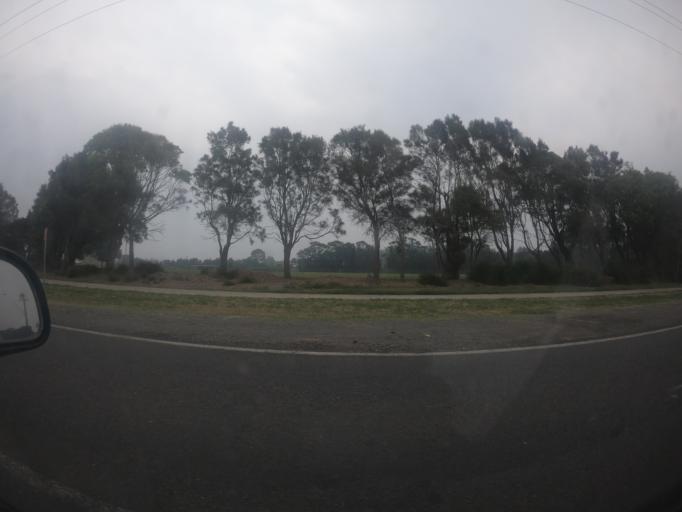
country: AU
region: New South Wales
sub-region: Shellharbour
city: Shellharbour Village
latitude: -34.5717
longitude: 150.8667
